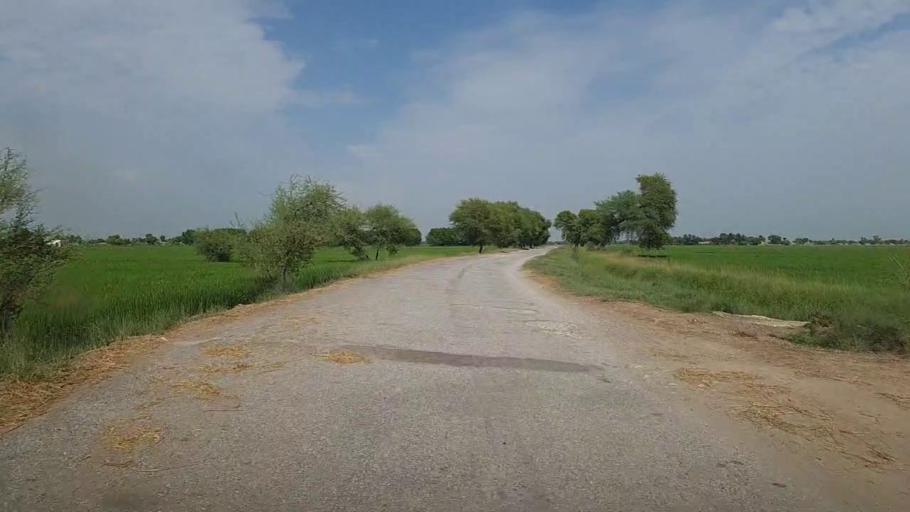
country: PK
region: Sindh
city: Thul
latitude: 28.2362
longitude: 68.7990
